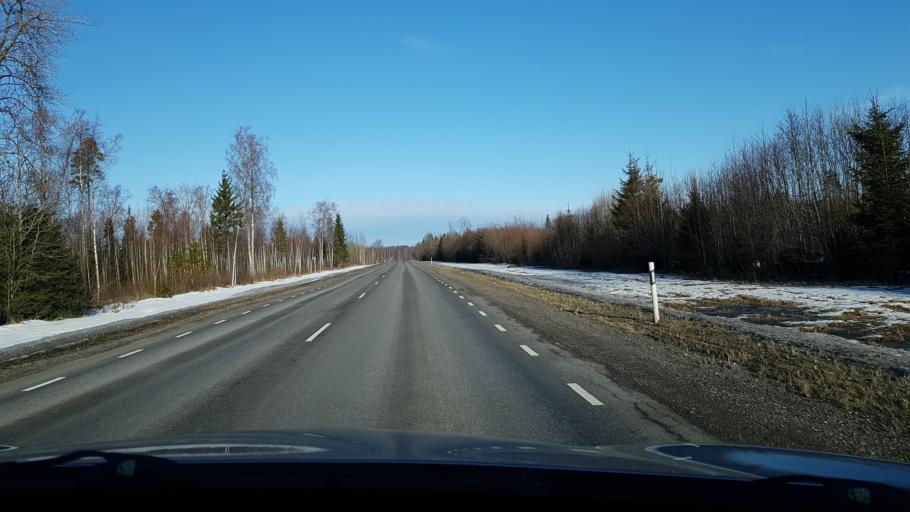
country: EE
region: Viljandimaa
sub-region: Vohma linn
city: Vohma
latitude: 58.6140
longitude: 25.5709
